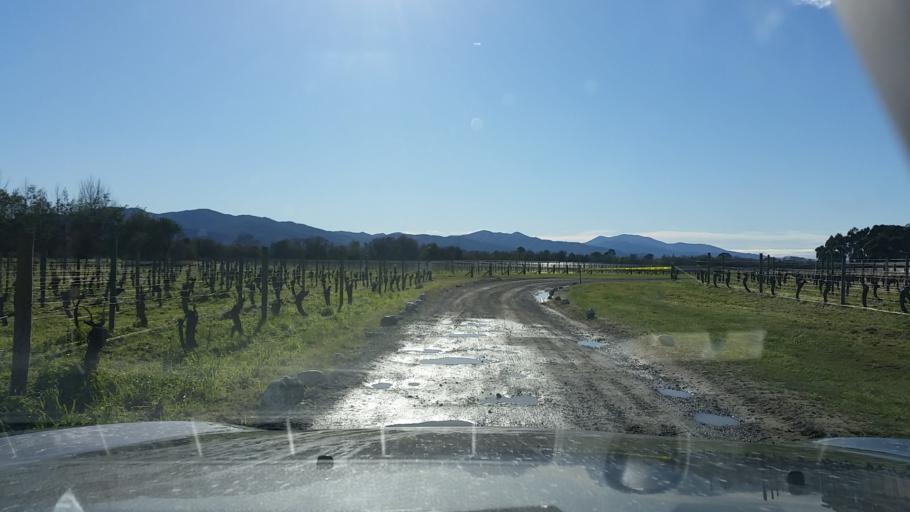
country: NZ
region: Marlborough
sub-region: Marlborough District
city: Blenheim
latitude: -41.5290
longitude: 173.8047
